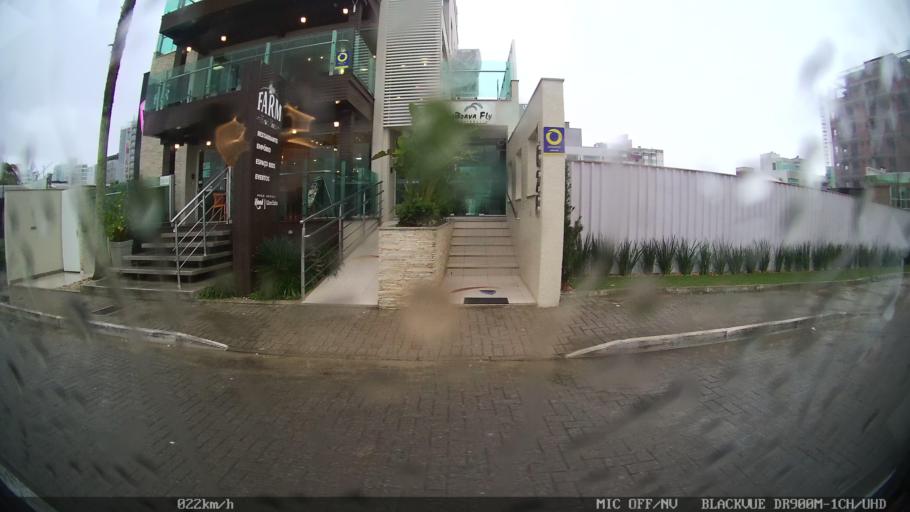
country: BR
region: Santa Catarina
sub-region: Balneario Camboriu
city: Balneario Camboriu
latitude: -26.9495
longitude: -48.6295
